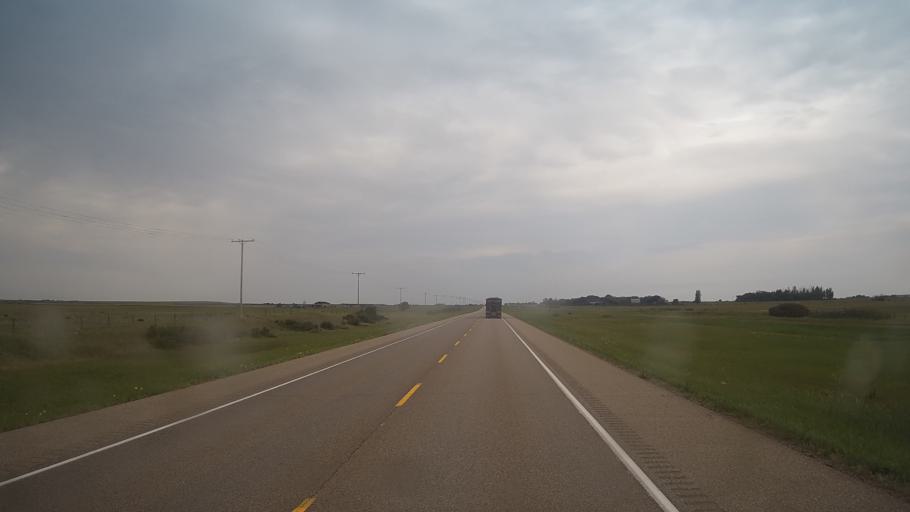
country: CA
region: Saskatchewan
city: Langham
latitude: 52.1289
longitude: -107.1559
